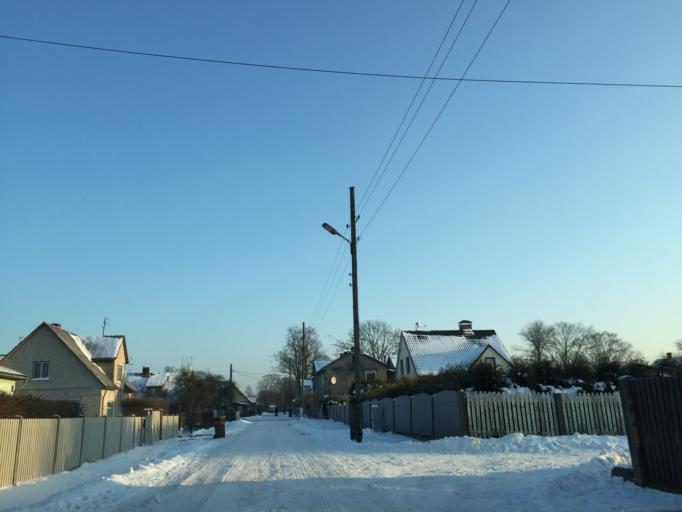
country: LV
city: Tireli
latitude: 56.9429
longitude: 23.6142
